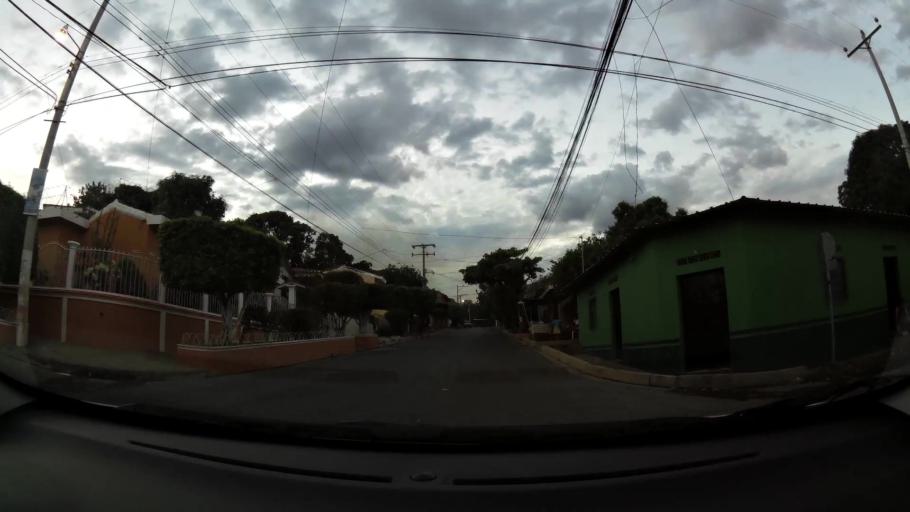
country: SV
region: San Vicente
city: San Vicente
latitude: 13.6419
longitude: -88.7915
